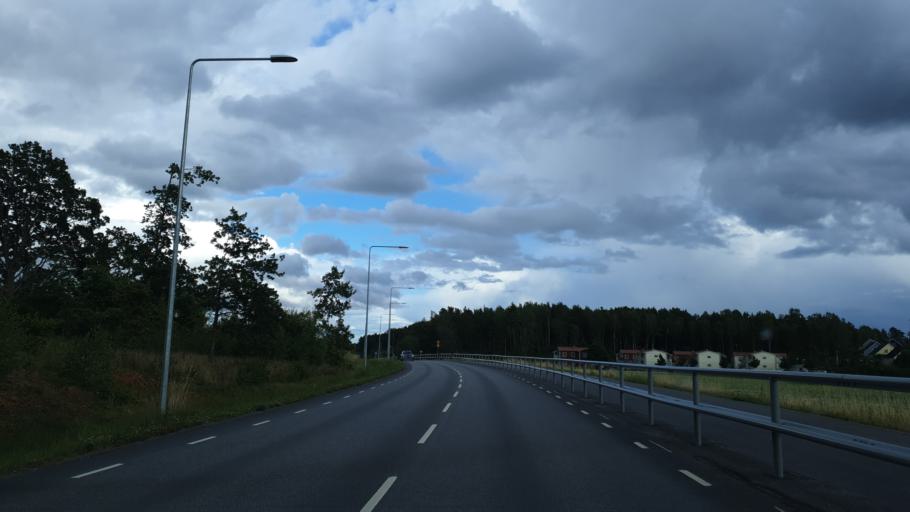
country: SE
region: Stockholm
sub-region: Jarfalla Kommun
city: Jakobsberg
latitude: 59.4245
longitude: 17.8009
